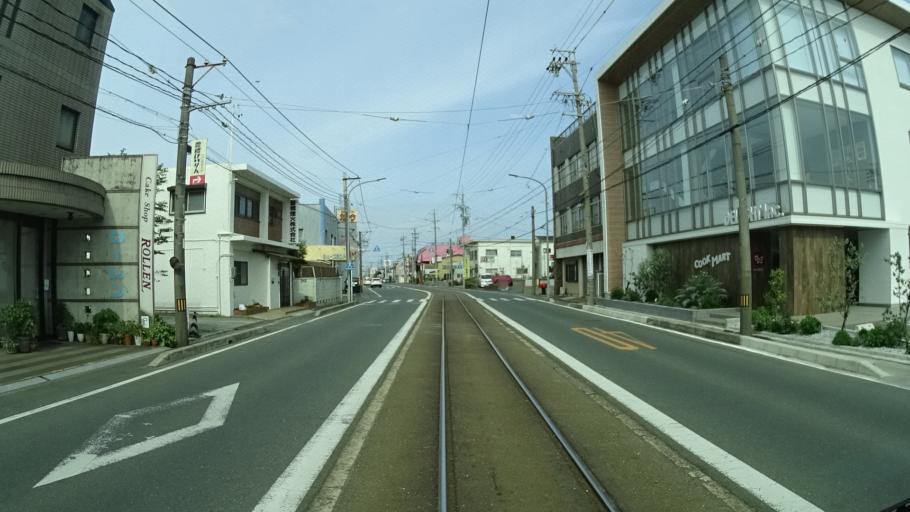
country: JP
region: Aichi
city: Toyohashi
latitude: 34.7649
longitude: 137.4185
